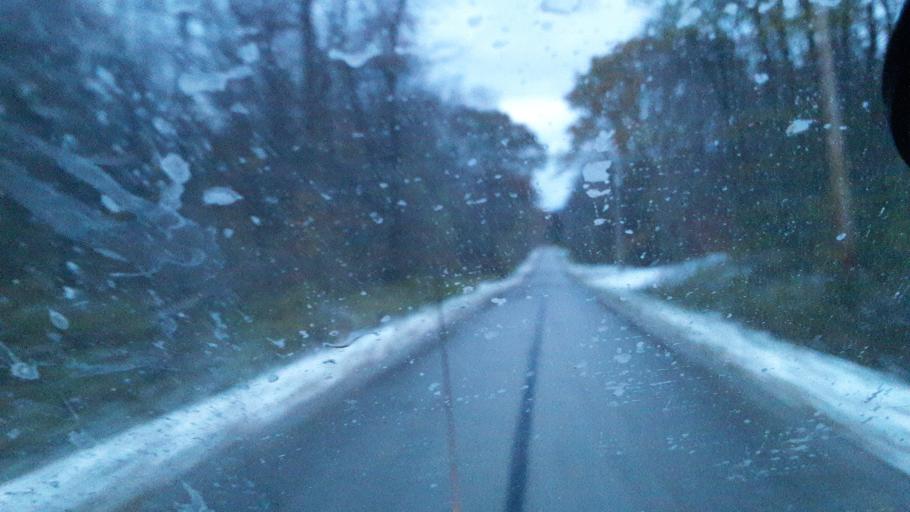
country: US
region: Ohio
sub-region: Portage County
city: Hiram
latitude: 41.3684
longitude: -81.1530
